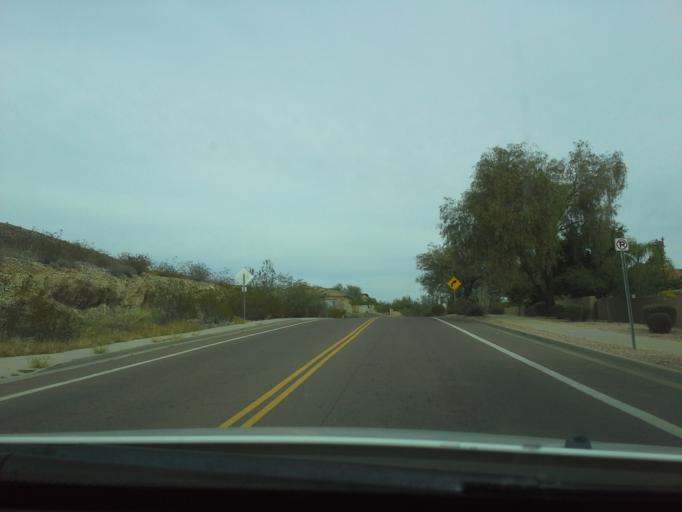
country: US
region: Arizona
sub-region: Maricopa County
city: Paradise Valley
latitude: 33.6118
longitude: -112.0219
